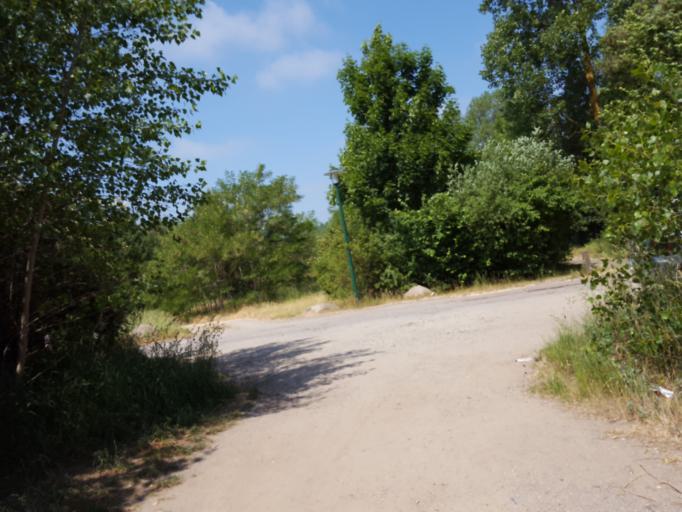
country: DE
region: Mecklenburg-Vorpommern
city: Kramerhof
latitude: 54.3242
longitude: 13.0482
